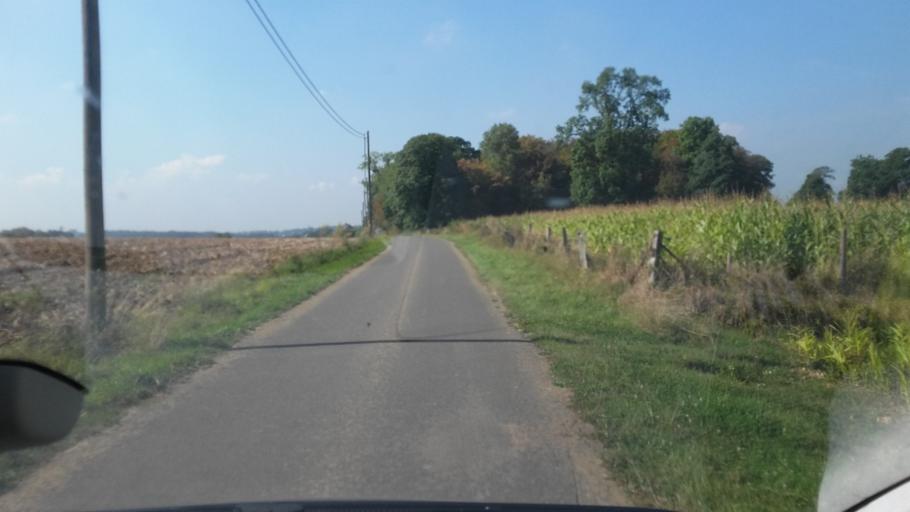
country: LU
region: Diekirch
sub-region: Canton de Redange
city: Beckerich
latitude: 49.7121
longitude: 5.8741
